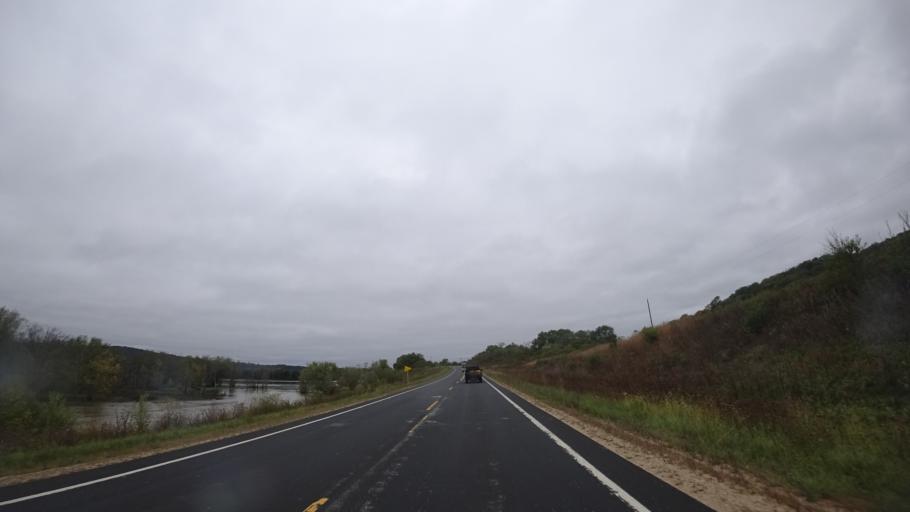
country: US
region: Wisconsin
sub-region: Grant County
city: Boscobel
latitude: 43.1158
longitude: -90.7906
